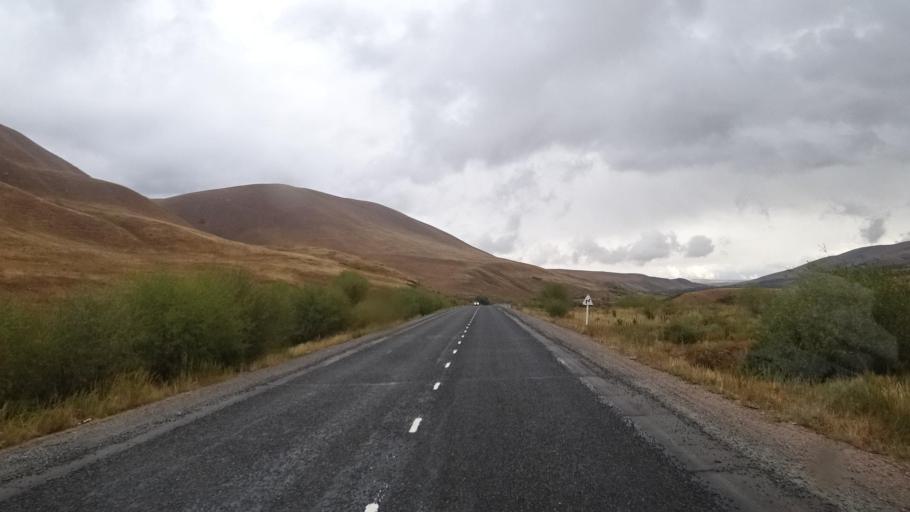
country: KG
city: Sosnovka
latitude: 42.2062
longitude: 73.6128
